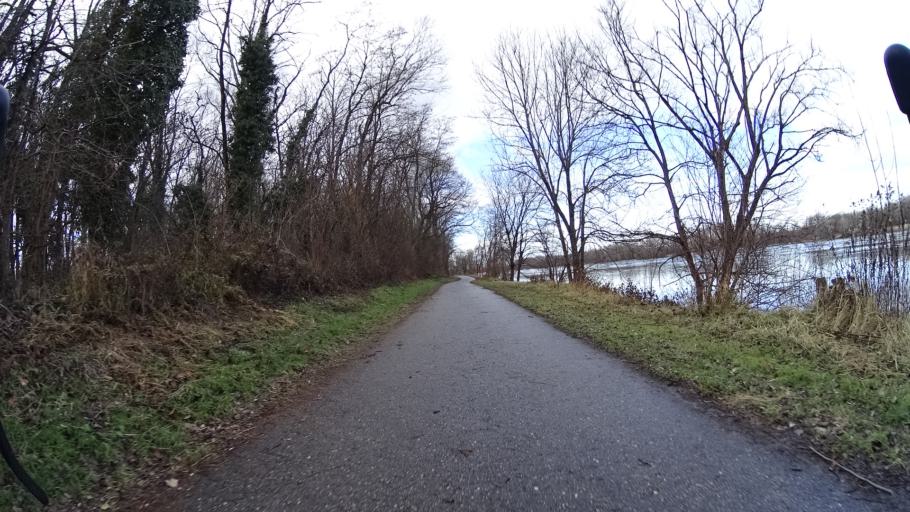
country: AT
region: Lower Austria
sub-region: Politischer Bezirk Tulln
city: Atzenbrugg
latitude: 48.3455
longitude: 15.9228
